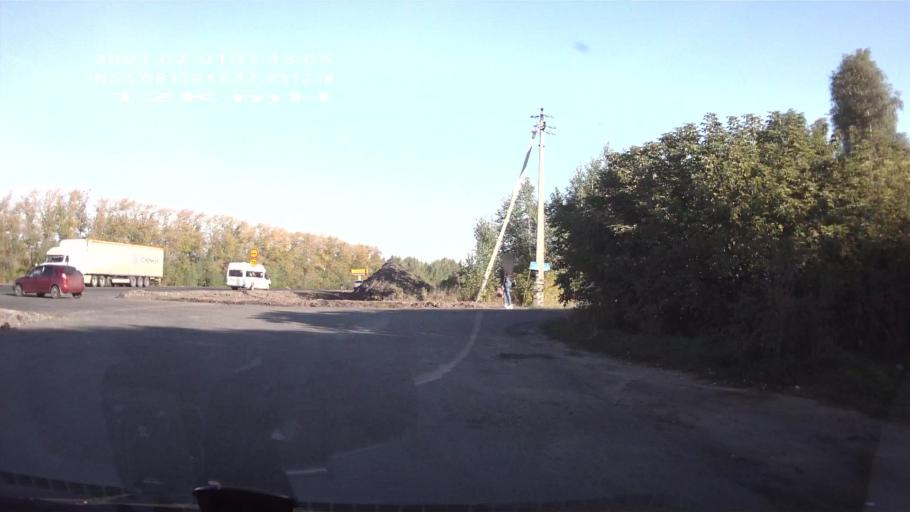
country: RU
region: Chuvashia
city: Shikhazany
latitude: 55.6813
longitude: 47.4320
